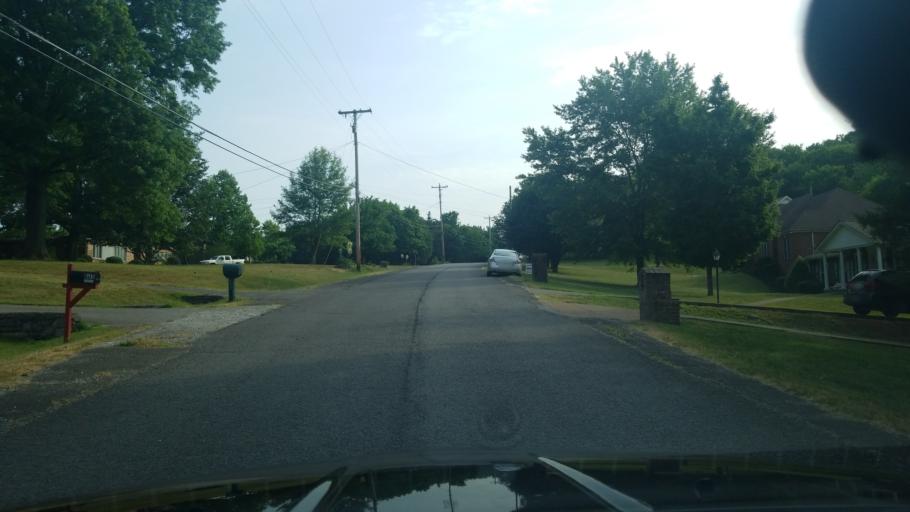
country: US
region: Tennessee
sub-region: Davidson County
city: Goodlettsville
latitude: 36.2780
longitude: -86.7464
